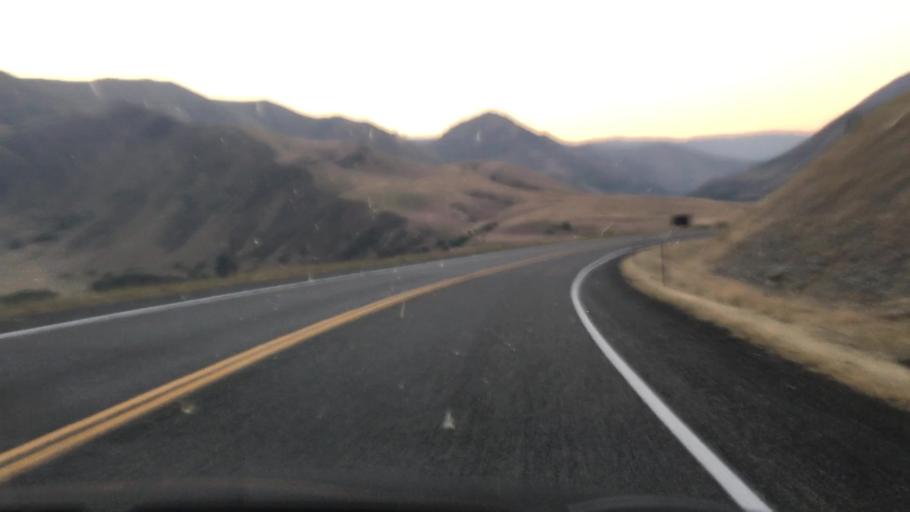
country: US
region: Idaho
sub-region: Idaho County
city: Grangeville
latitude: 45.6753
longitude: -116.3092
